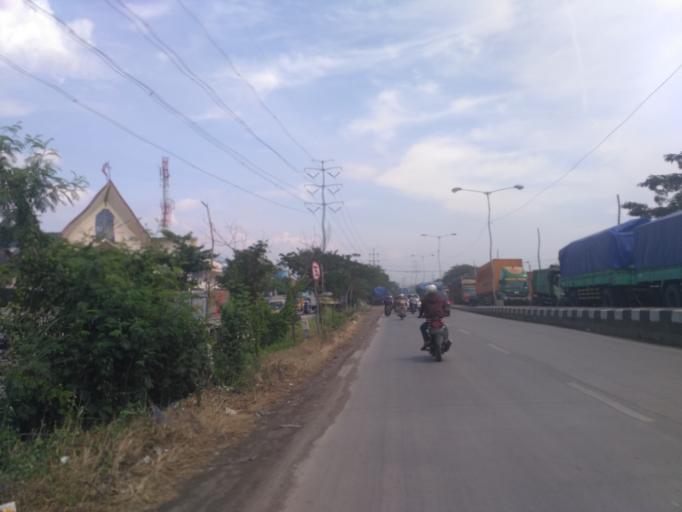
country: ID
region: Central Java
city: Semarang
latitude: -6.9534
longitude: 110.4075
